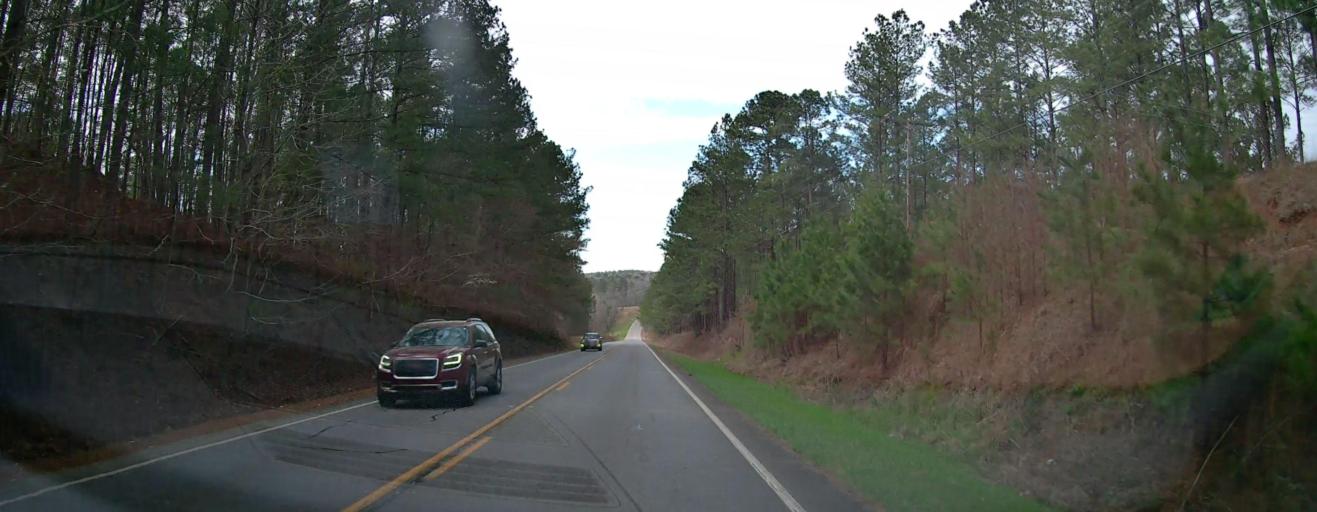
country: US
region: Georgia
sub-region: Jones County
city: Gray
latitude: 32.9964
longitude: -83.6900
